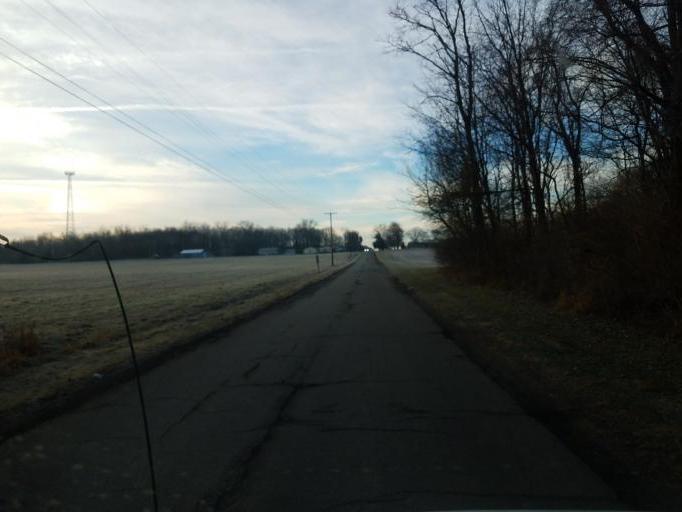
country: US
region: Ohio
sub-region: Morrow County
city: Mount Gilead
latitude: 40.5513
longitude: -82.8628
